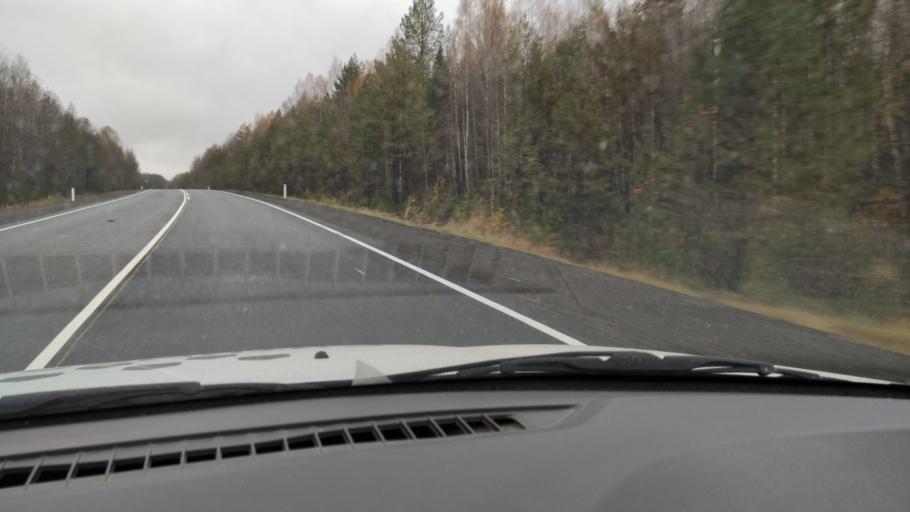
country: RU
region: Kirov
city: Chernaya Kholunitsa
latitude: 58.8761
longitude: 51.4818
